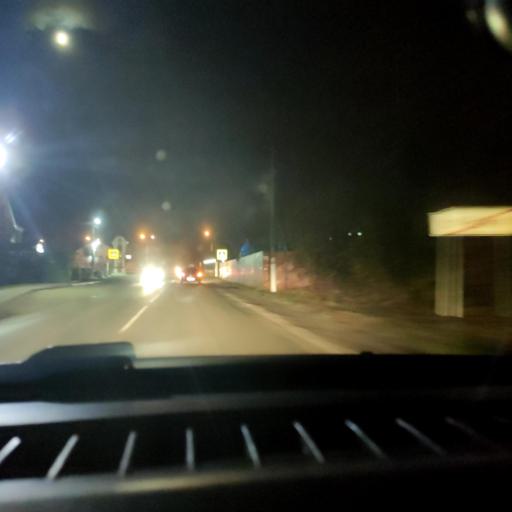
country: RU
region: Voronezj
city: Novaya Usman'
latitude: 51.6366
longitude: 39.3326
